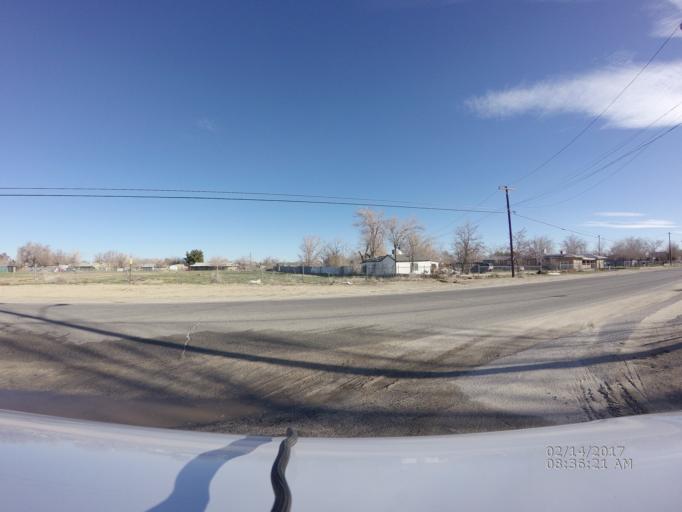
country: US
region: California
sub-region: Los Angeles County
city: Littlerock
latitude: 34.5579
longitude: -117.9451
